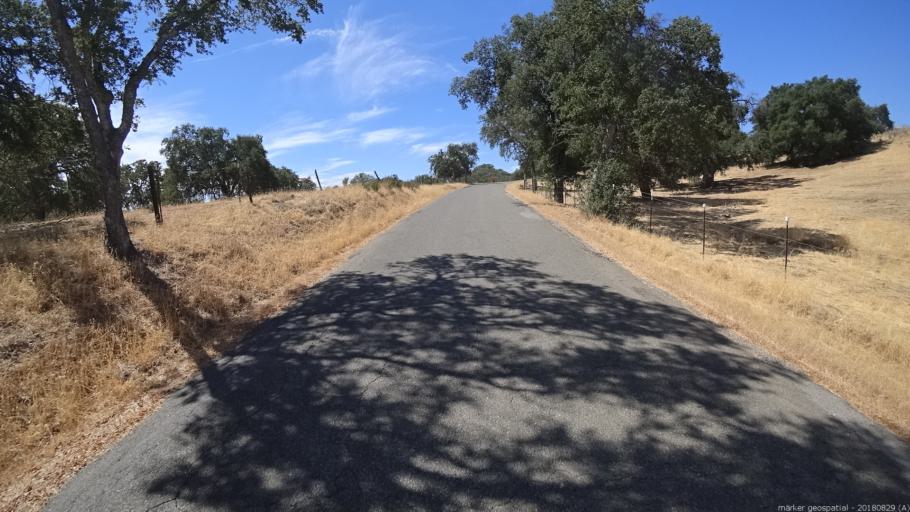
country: US
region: California
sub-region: San Luis Obispo County
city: Lake Nacimiento
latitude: 35.8181
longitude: -121.0534
